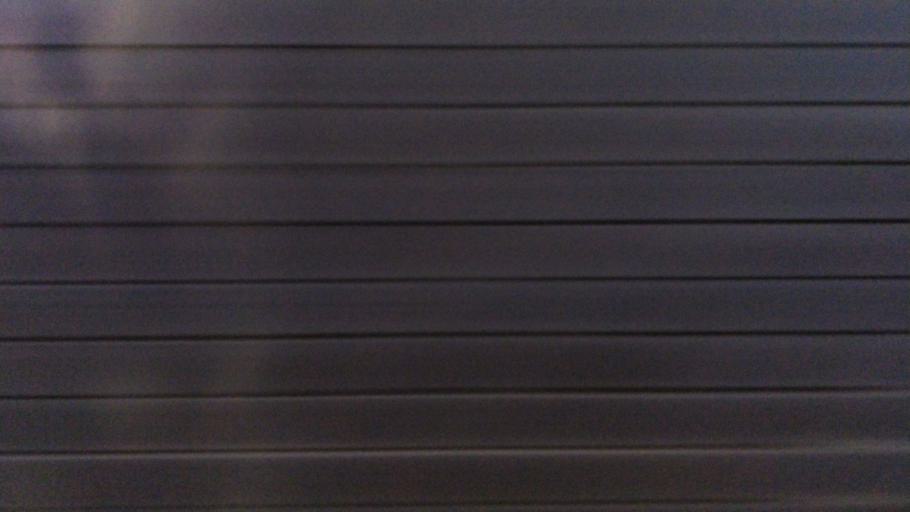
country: GB
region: England
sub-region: Manchester
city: Swinton
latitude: 53.5160
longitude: -2.3461
